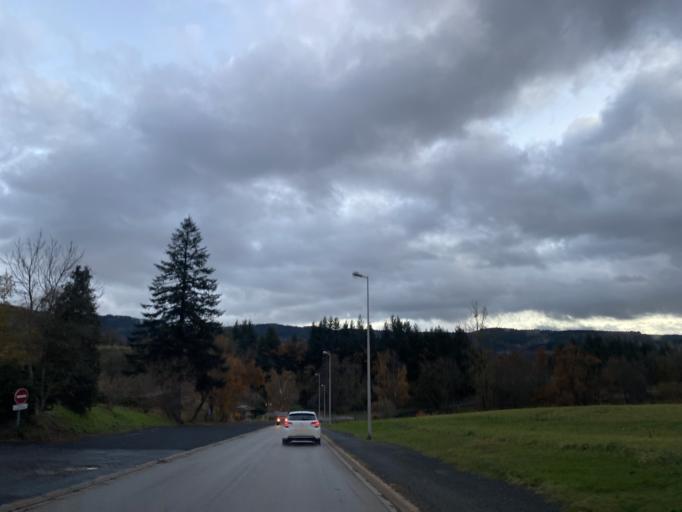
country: FR
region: Auvergne
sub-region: Departement du Puy-de-Dome
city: Cunlhat
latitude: 45.6261
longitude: 3.5621
